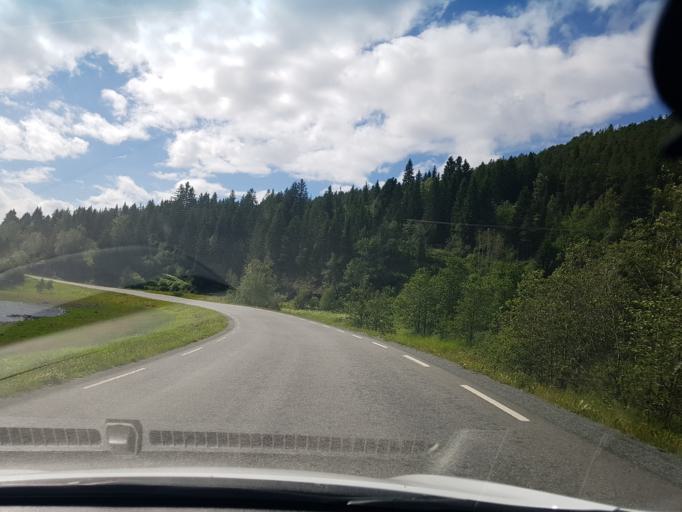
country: NO
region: Nord-Trondelag
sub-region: Stjordal
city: Stjordal
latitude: 63.6160
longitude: 10.9115
